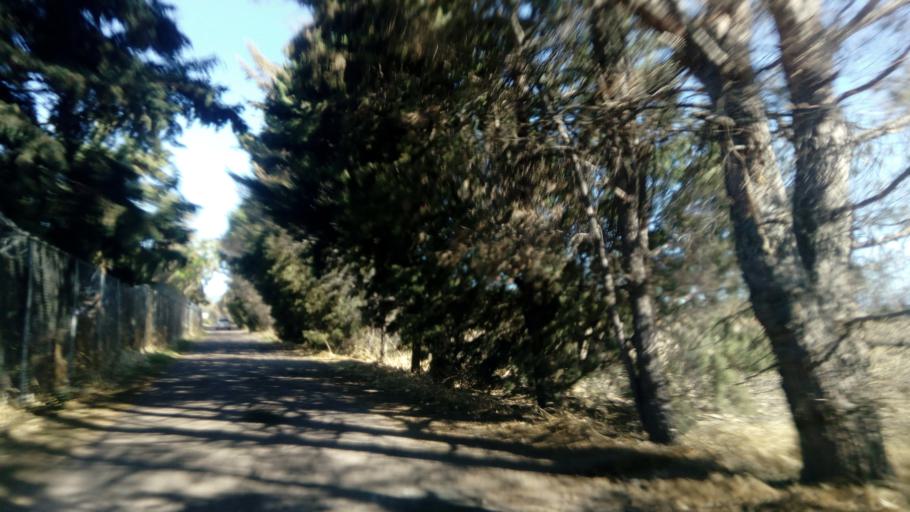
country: MX
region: Durango
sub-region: Durango
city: Jose Refugio Salcido
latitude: 24.0119
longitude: -104.5526
